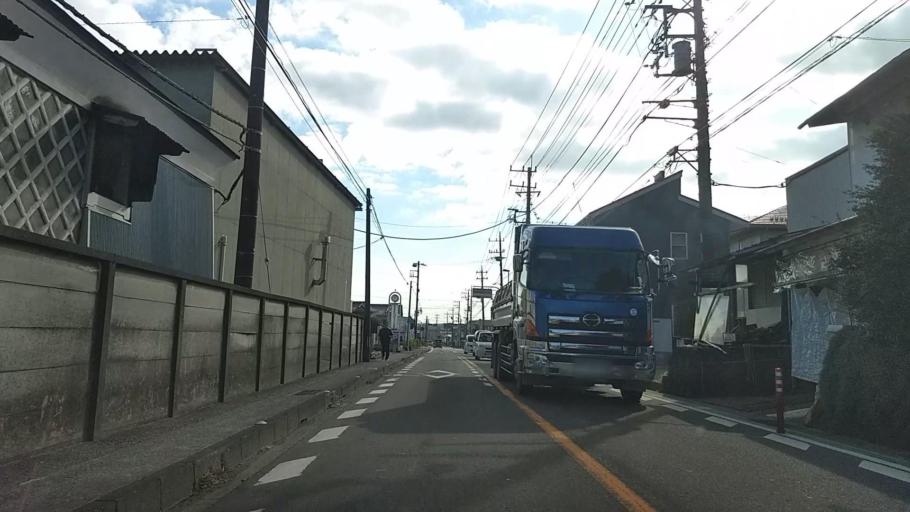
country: JP
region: Kanagawa
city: Isehara
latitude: 35.4437
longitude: 139.2981
